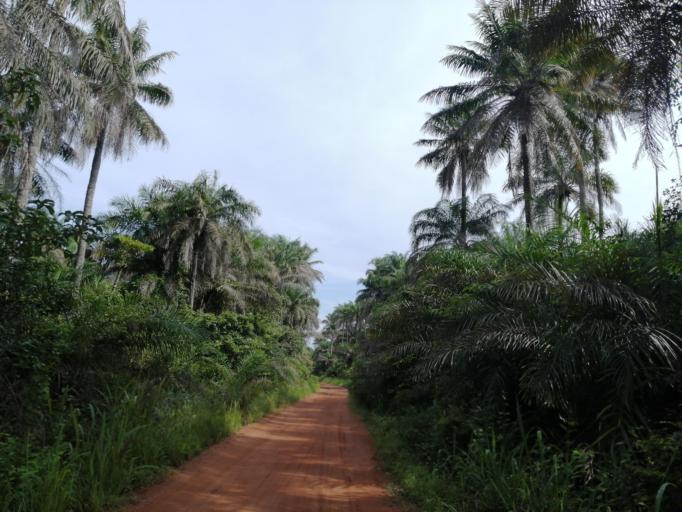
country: SL
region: Northern Province
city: Port Loko
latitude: 8.7828
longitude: -12.9226
